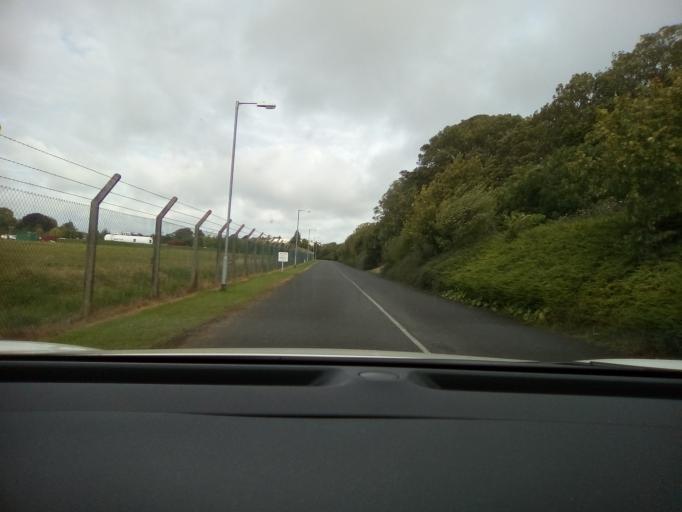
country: IE
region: Leinster
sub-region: Kildare
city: Leixlip
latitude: 53.3565
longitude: -6.4848
